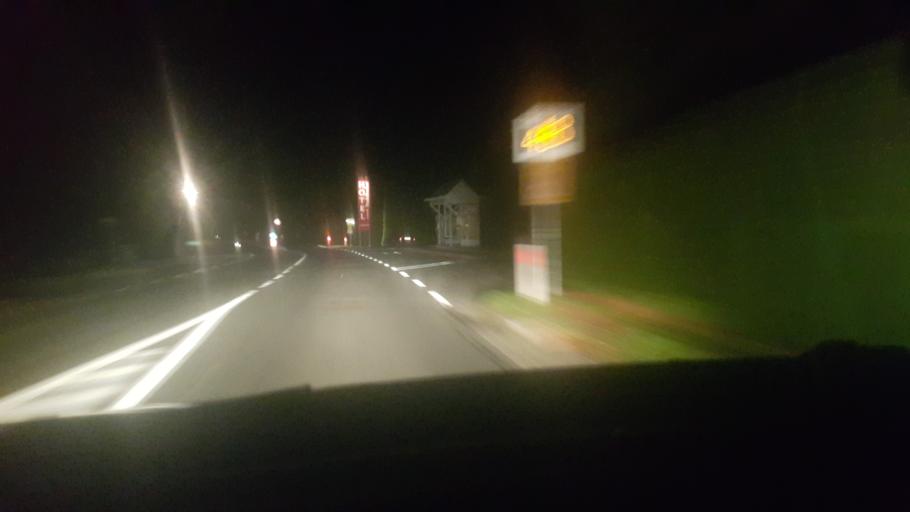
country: AT
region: Carinthia
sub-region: Politischer Bezirk Feldkirchen
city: Feldkirchen in Karnten
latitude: 46.7025
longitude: 14.1090
